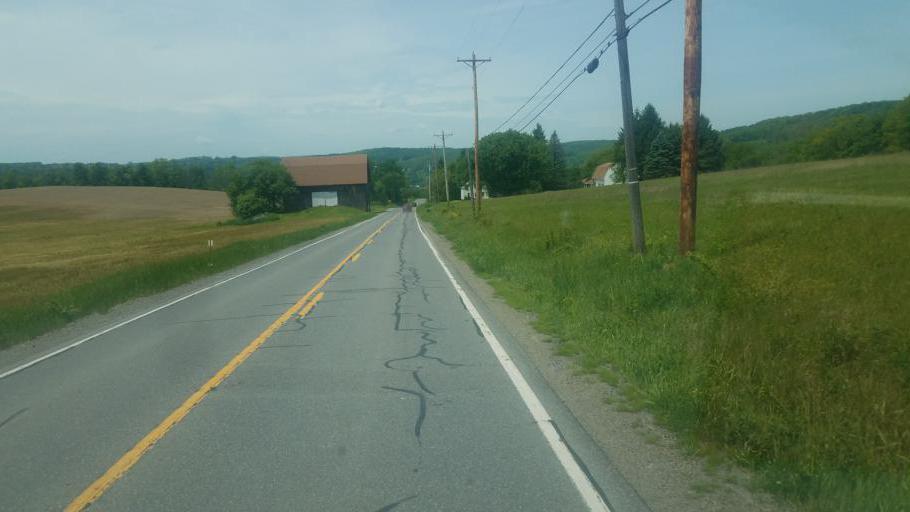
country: US
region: Pennsylvania
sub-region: Tioga County
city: Wellsboro
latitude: 41.7701
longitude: -77.2219
